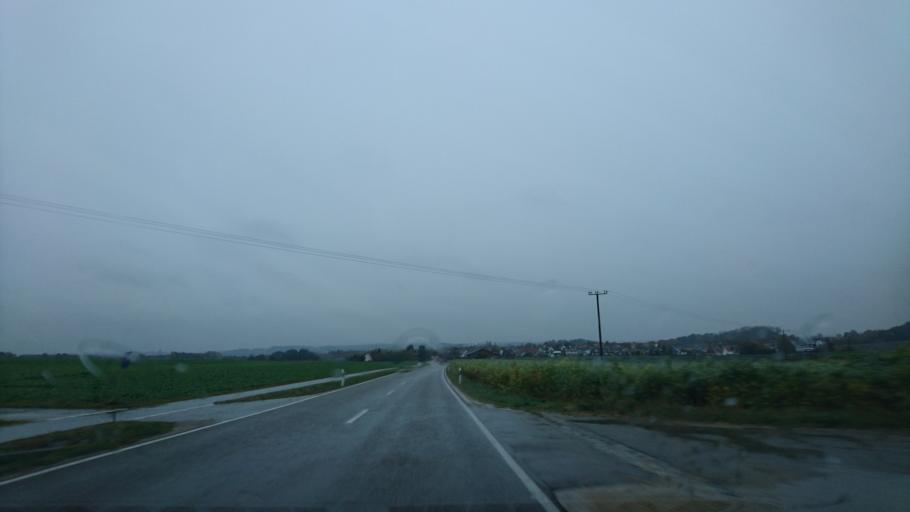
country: DE
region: Bavaria
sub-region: Swabia
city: Aichach
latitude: 48.4545
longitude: 11.1653
